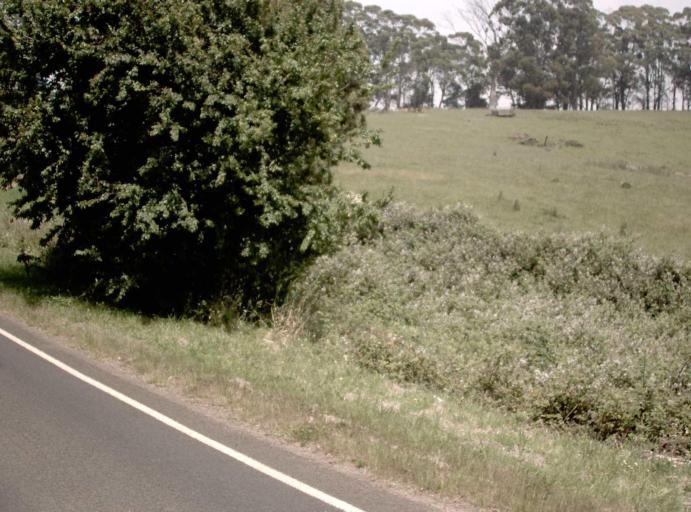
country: AU
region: Victoria
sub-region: Latrobe
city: Traralgon
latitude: -38.3594
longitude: 146.7225
